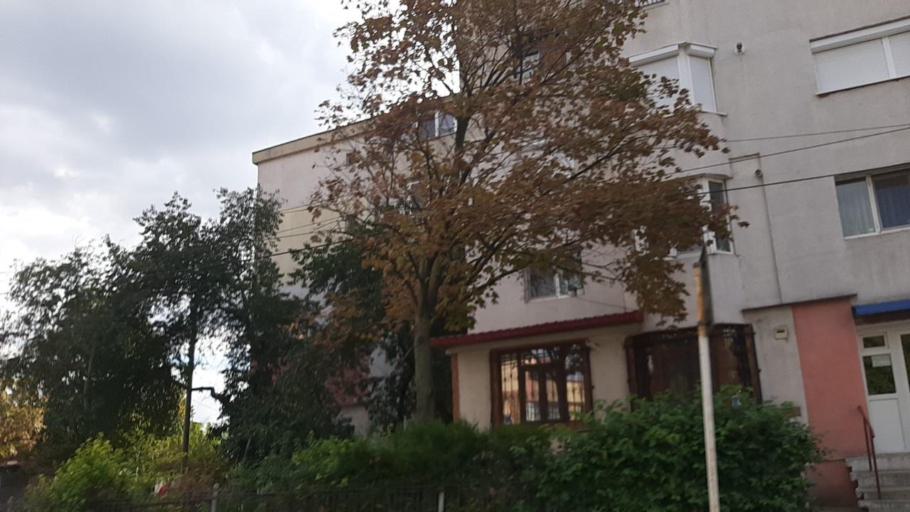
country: RO
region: Galati
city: Galati
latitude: 45.4482
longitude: 28.0294
